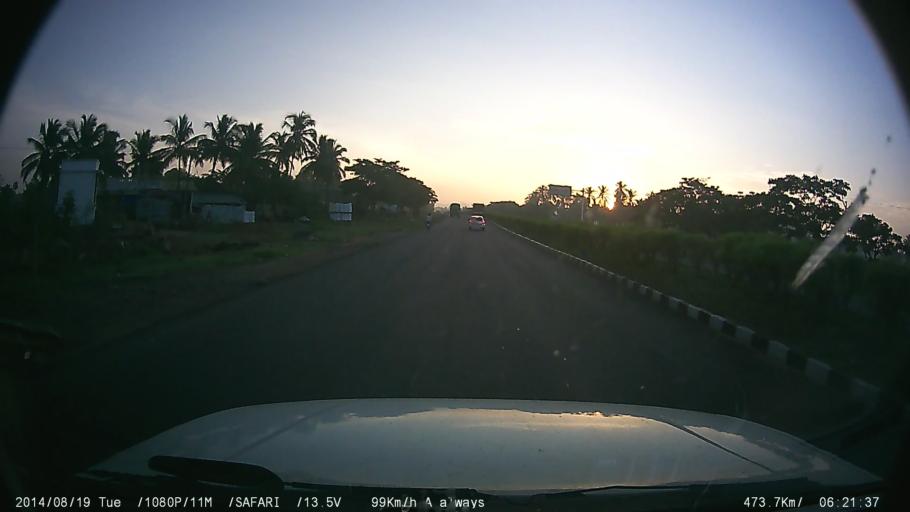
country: IN
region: Tamil Nadu
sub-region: Dharmapuri
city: Dharmapuri
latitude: 12.0187
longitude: 78.0915
